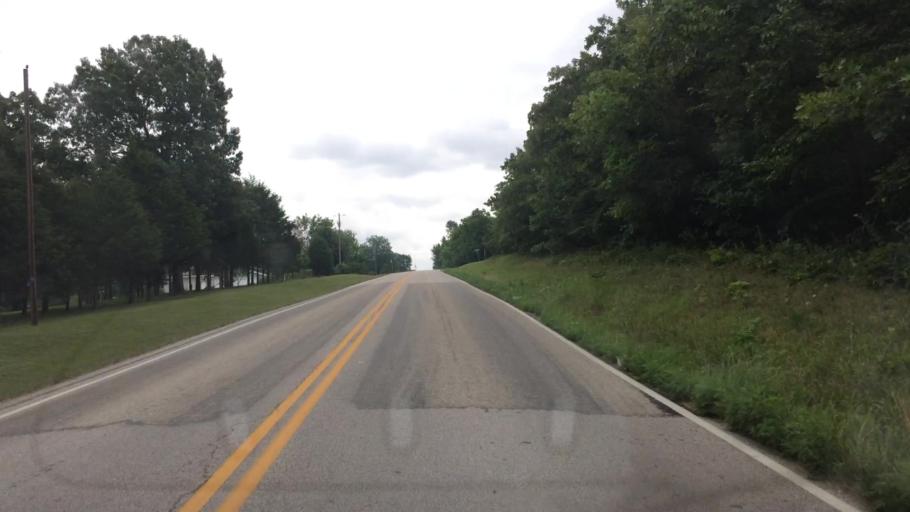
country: US
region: Missouri
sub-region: Webster County
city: Marshfield
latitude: 37.3414
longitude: -93.0083
